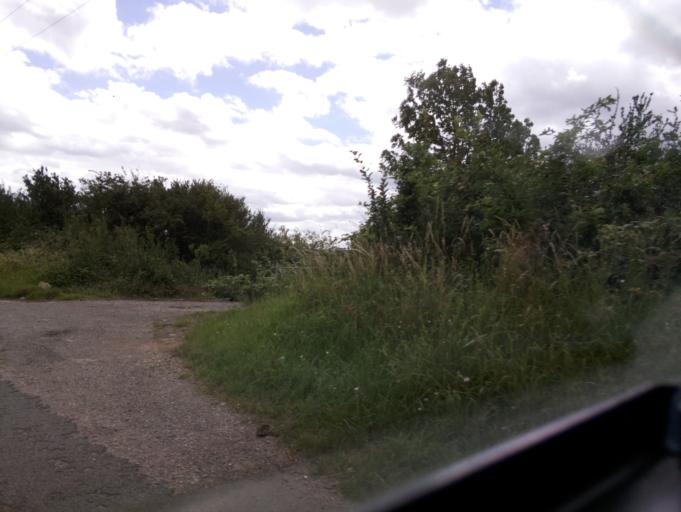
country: GB
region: England
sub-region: Nottinghamshire
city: West Bridgford
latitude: 52.9247
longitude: -1.0955
